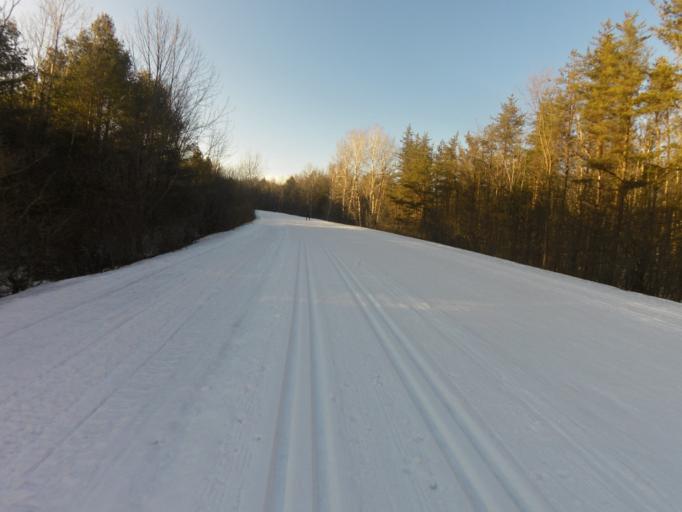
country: CA
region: Quebec
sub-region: Outaouais
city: Gatineau
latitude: 45.5140
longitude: -75.8231
